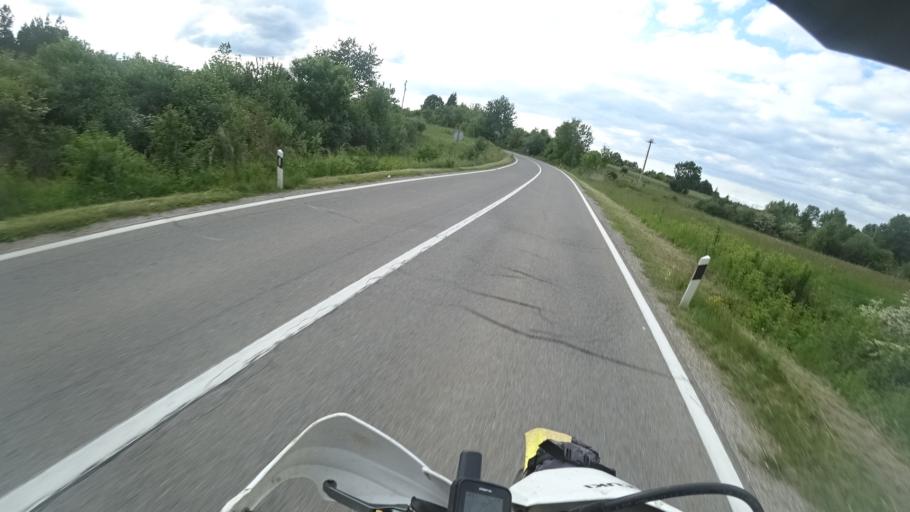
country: HR
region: Licko-Senjska
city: Gospic
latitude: 44.5125
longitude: 15.4263
